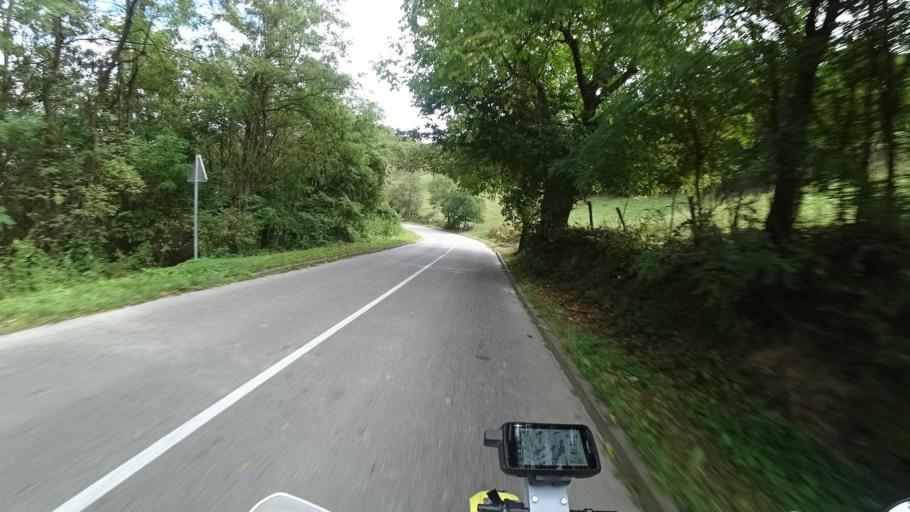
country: BA
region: Federation of Bosnia and Herzegovina
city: Buzim
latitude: 45.0208
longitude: 16.0362
